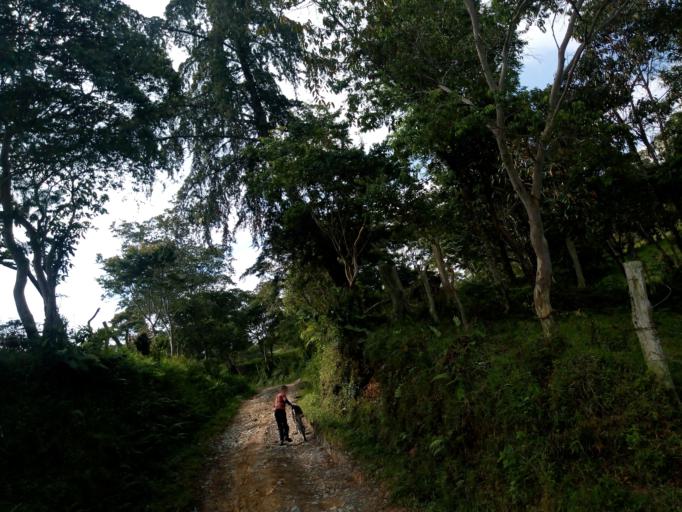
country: CO
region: Boyaca
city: Moniquira
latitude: 5.8688
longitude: -73.5017
